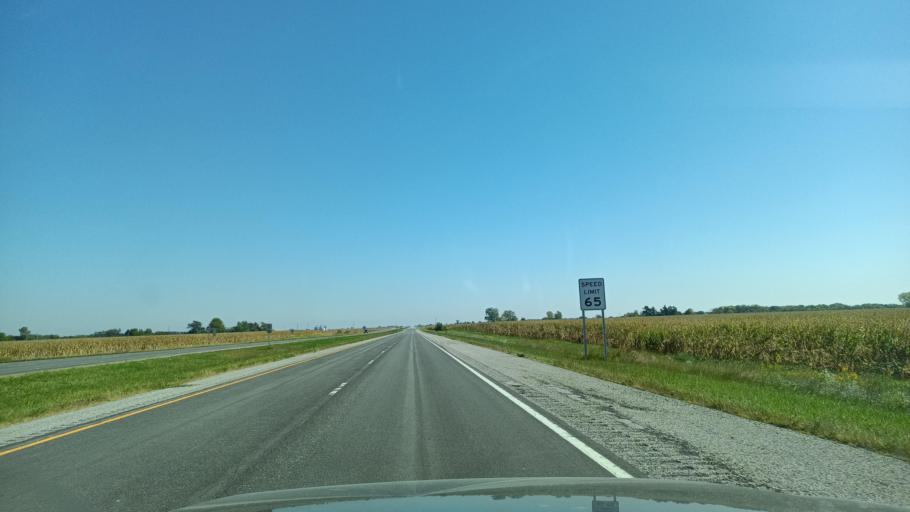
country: US
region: Illinois
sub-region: Adams County
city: Camp Point
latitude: 40.1851
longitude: -91.1820
